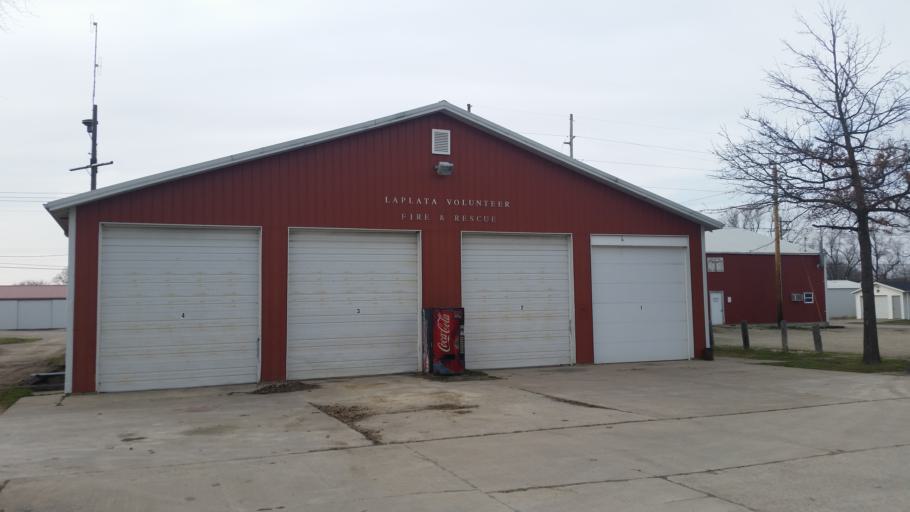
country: US
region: Missouri
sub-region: Macon County
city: La Plata
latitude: 40.0239
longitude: -92.4887
